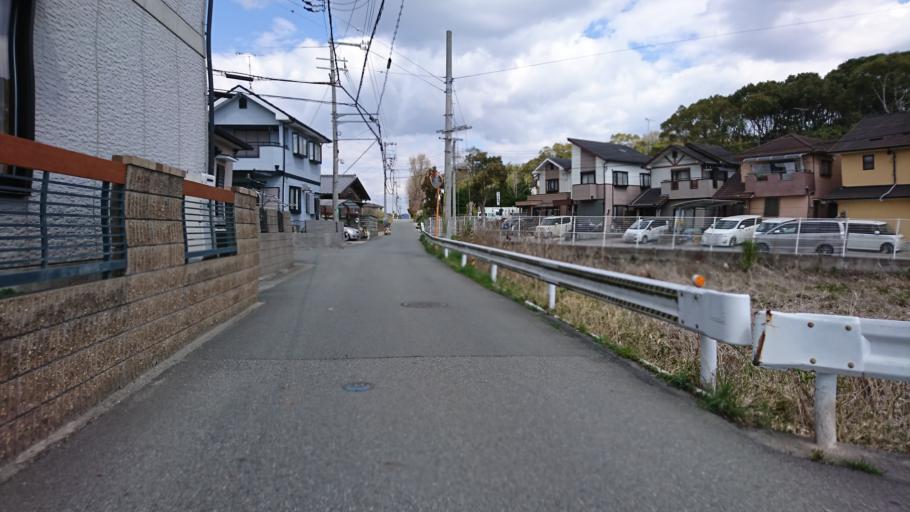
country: JP
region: Hyogo
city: Kakogawacho-honmachi
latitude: 34.7734
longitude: 134.8719
